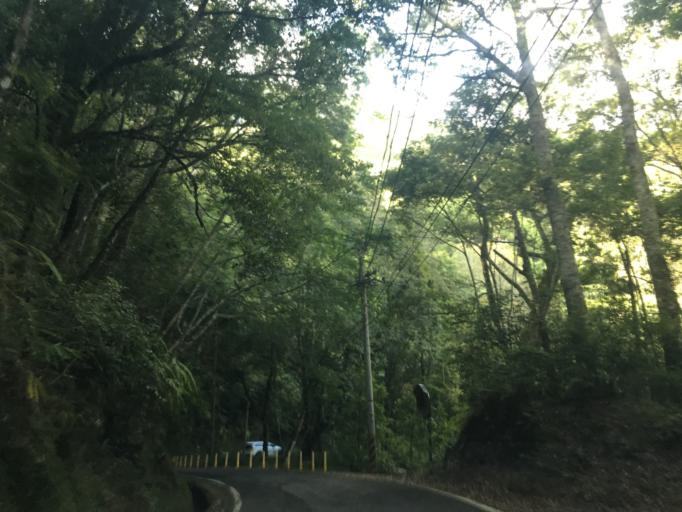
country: TW
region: Taiwan
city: Fengyuan
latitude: 24.2270
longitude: 120.9761
